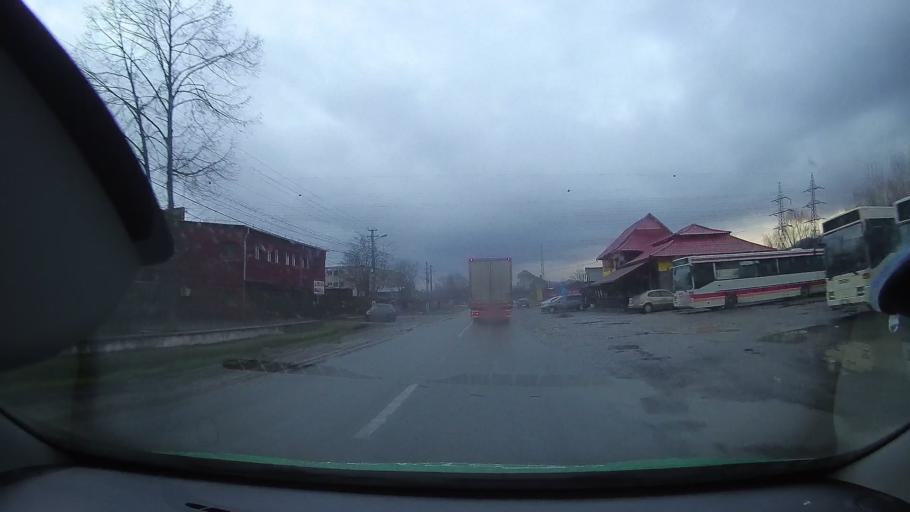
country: RO
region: Hunedoara
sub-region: Municipiul Brad
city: Brad
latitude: 46.1436
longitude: 22.7749
